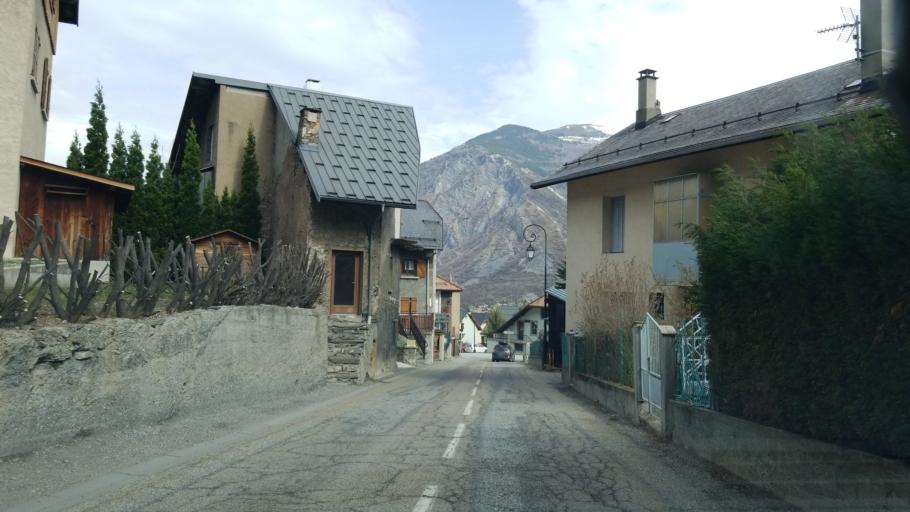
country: FR
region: Rhone-Alpes
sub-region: Departement de la Savoie
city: Villargondran
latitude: 45.2457
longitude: 6.4020
